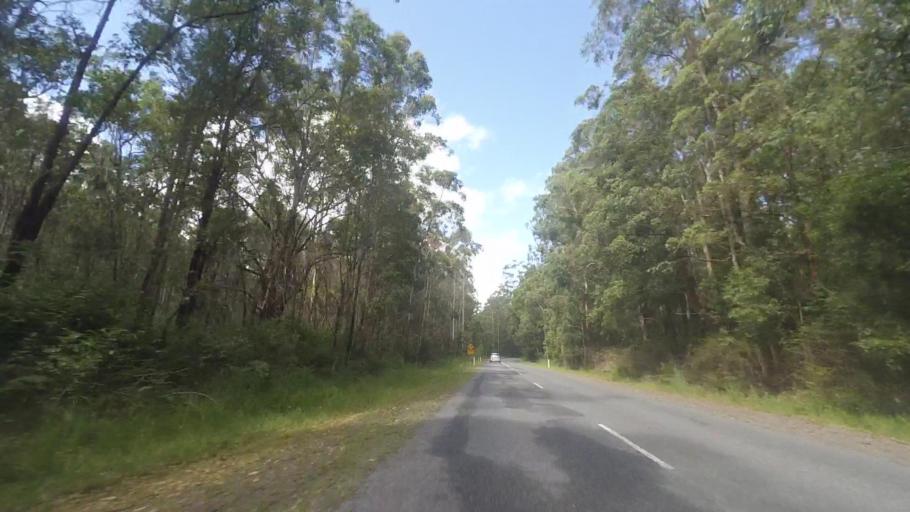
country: AU
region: New South Wales
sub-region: Great Lakes
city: Bulahdelah
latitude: -32.4016
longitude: 152.2838
